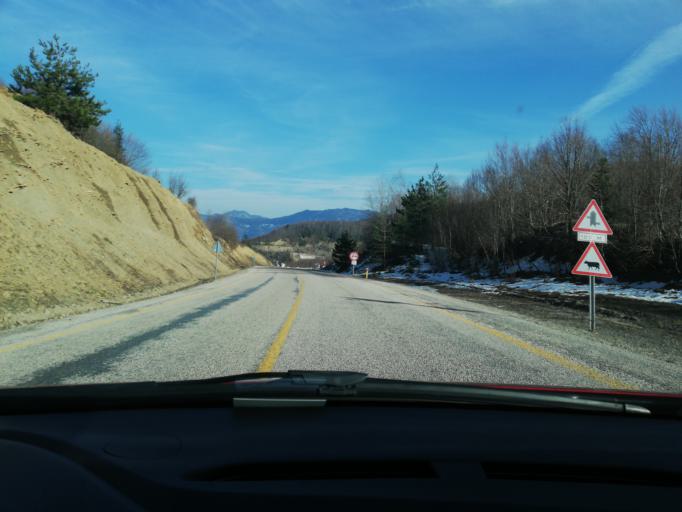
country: TR
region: Kastamonu
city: Senpazar
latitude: 41.7928
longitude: 33.1188
